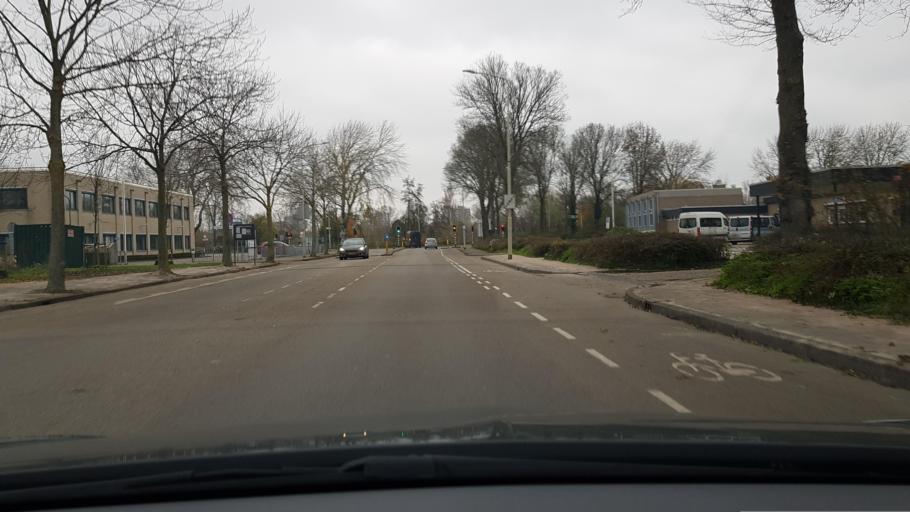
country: NL
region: North Holland
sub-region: Gemeente Haarlem
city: Haarlem
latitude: 52.3667
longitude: 4.6643
